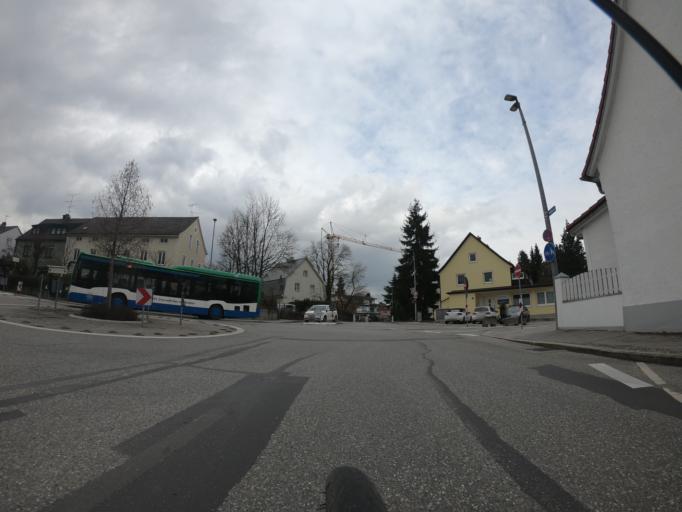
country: DE
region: Bavaria
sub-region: Upper Bavaria
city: Fuerstenfeldbruck
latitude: 48.1761
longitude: 11.2444
